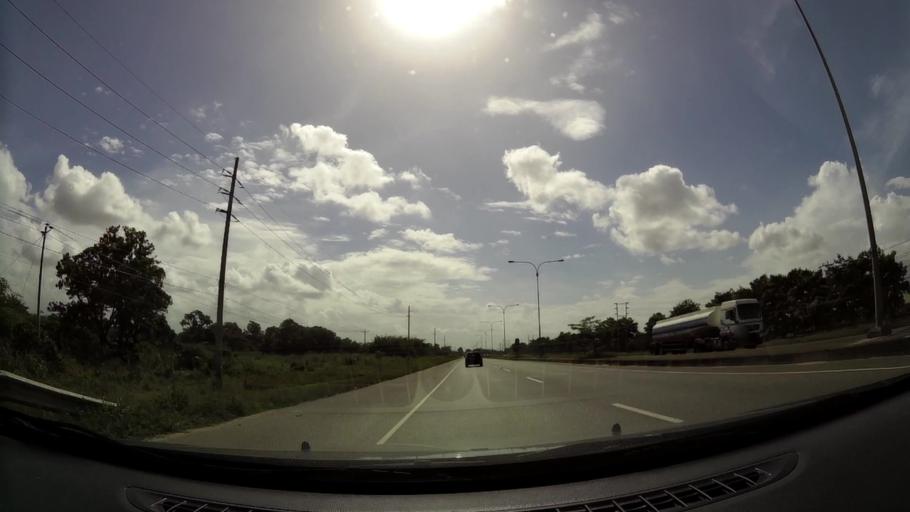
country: TT
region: Borough of Arima
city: Arima
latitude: 10.6121
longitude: -61.2638
